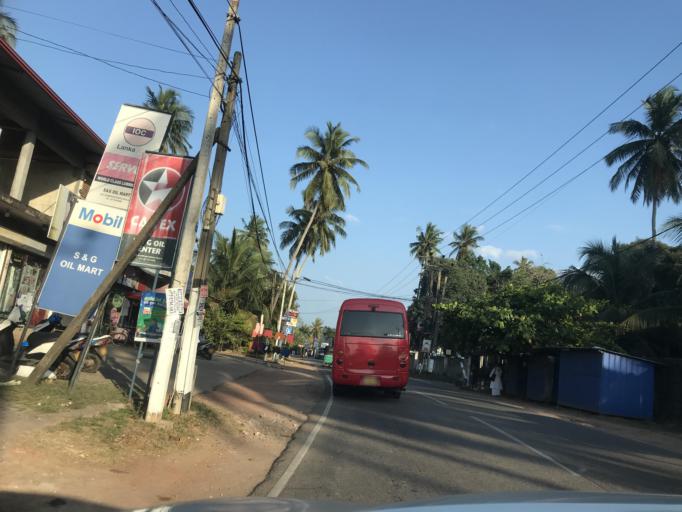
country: LK
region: Western
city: Ja Ela
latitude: 7.1011
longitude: 79.9140
